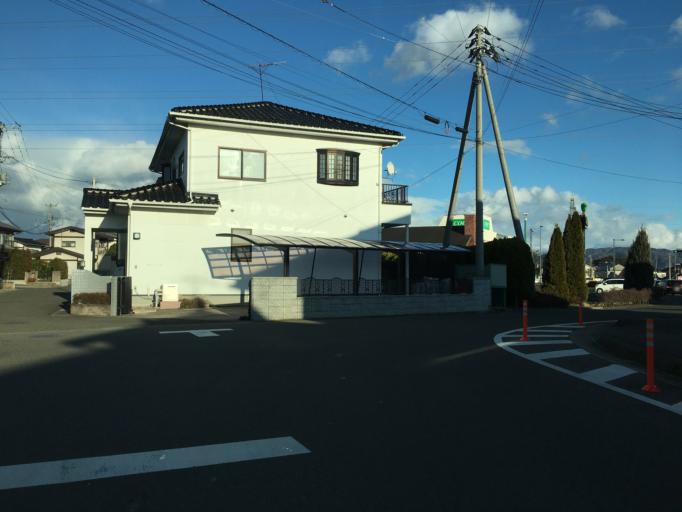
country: JP
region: Fukushima
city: Fukushima-shi
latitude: 37.7726
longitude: 140.4394
